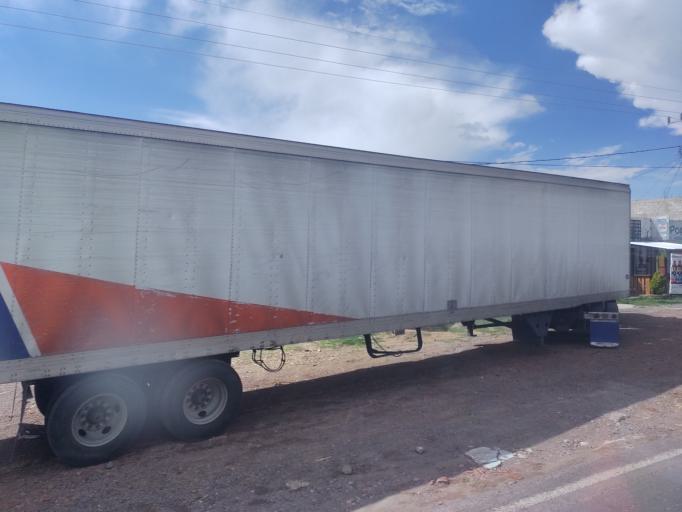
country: MX
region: Mexico
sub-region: Aculco
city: El Colorado
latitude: 20.0950
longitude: -99.7661
